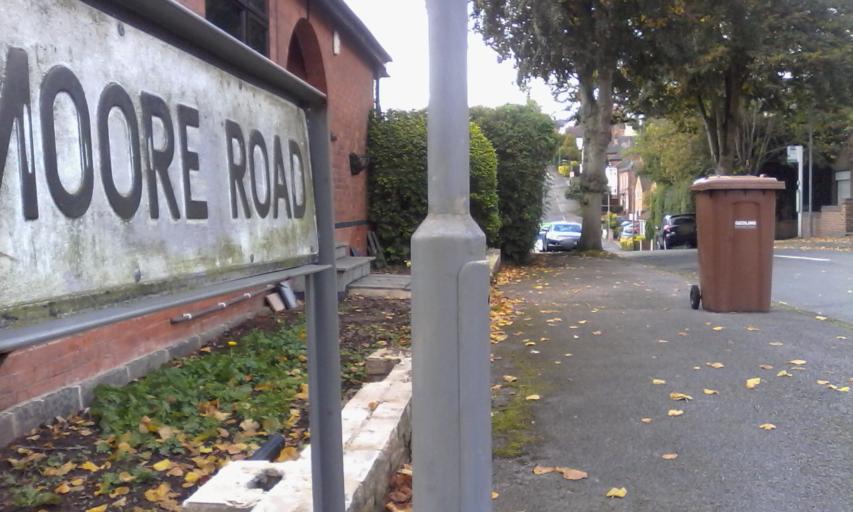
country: GB
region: England
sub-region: Nottinghamshire
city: Arnold
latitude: 52.9794
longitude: -1.1198
